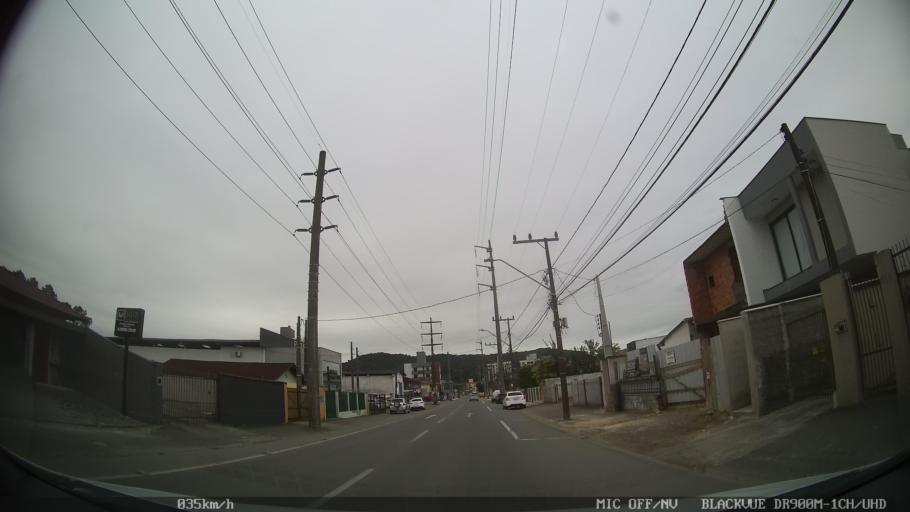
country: BR
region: Santa Catarina
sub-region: Joinville
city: Joinville
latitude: -26.2674
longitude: -48.8495
